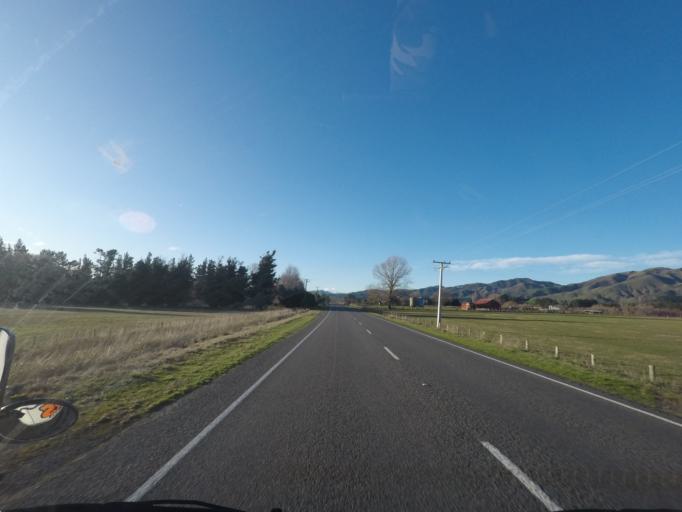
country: NZ
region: Canterbury
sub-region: Kaikoura District
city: Kaikoura
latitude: -42.7171
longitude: 173.2879
